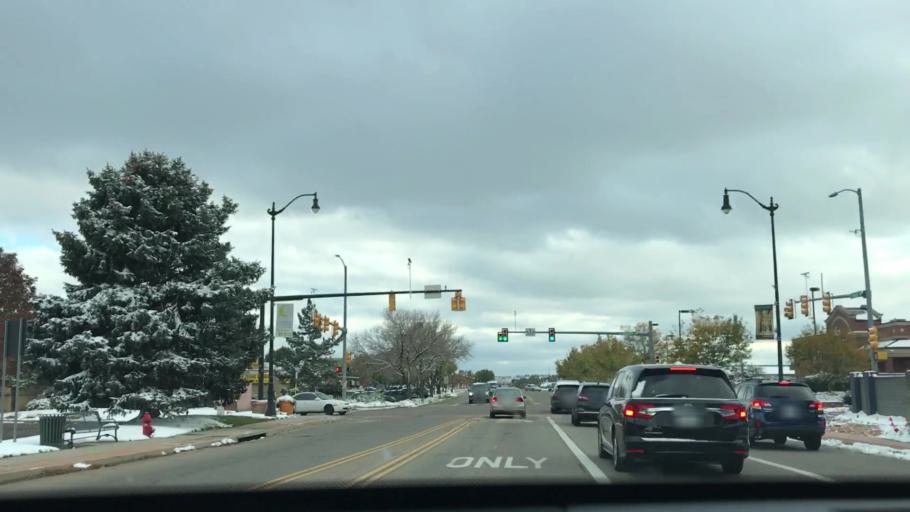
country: US
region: Colorado
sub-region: Boulder County
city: Lafayette
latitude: 39.9875
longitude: -105.0905
